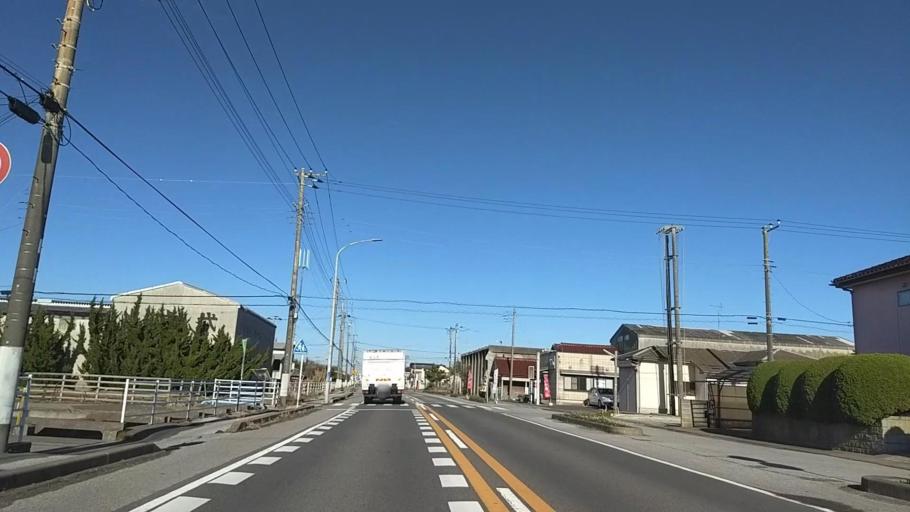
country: JP
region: Chiba
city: Naruto
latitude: 35.5229
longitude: 140.4441
